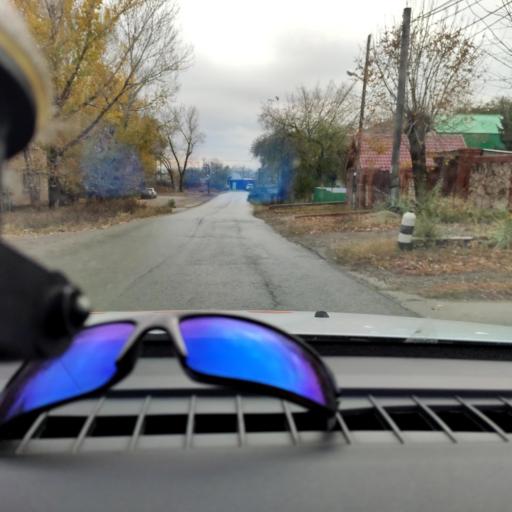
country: RU
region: Samara
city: Samara
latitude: 53.1807
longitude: 50.2018
